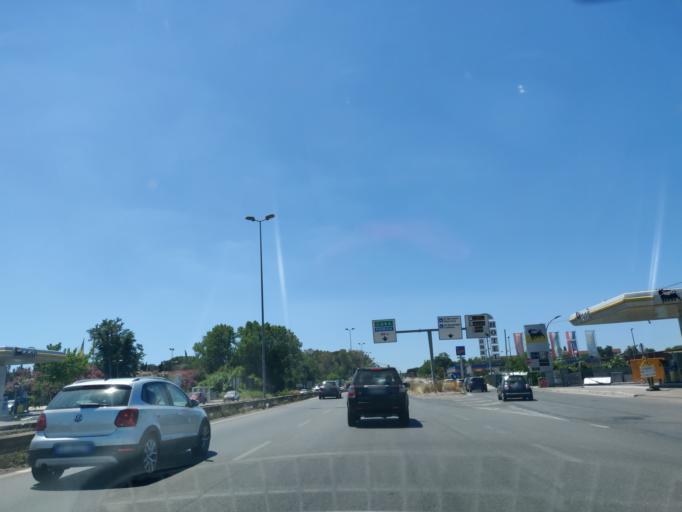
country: IT
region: Latium
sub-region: Citta metropolitana di Roma Capitale
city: Selcetta
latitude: 41.8176
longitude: 12.4625
